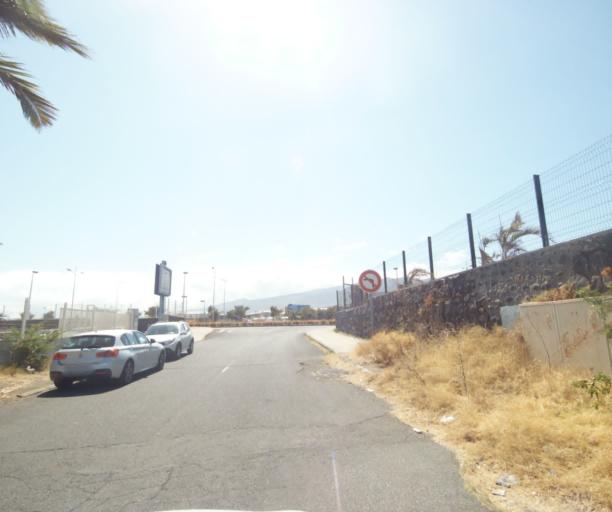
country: RE
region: Reunion
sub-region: Reunion
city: Le Port
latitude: -20.9619
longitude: 55.2932
